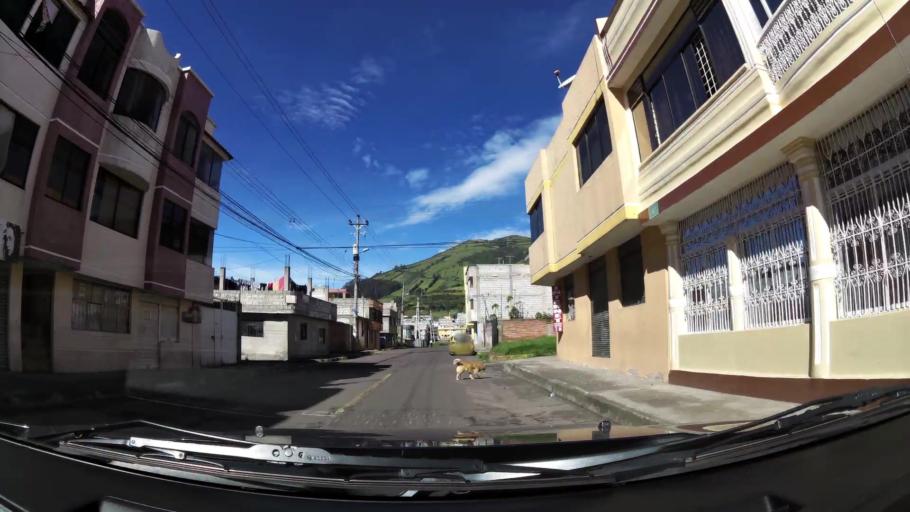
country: EC
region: Pichincha
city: Quito
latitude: -0.2963
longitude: -78.5693
